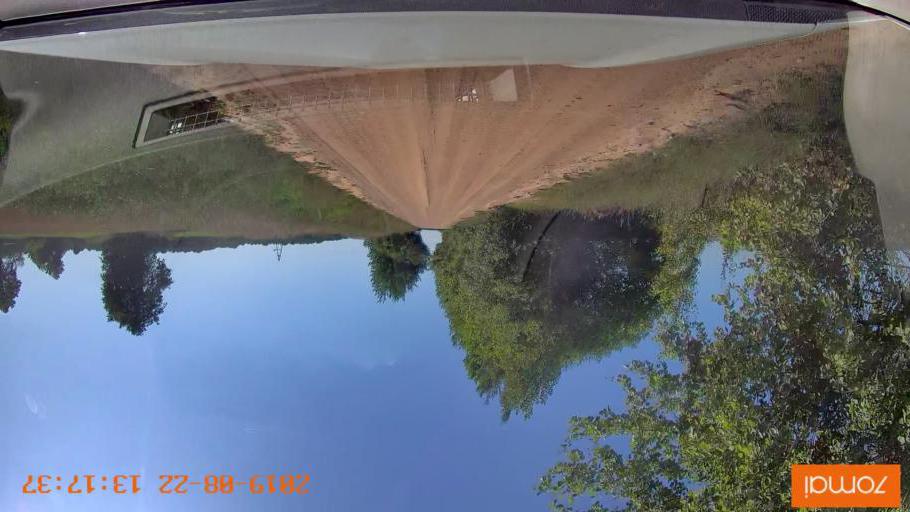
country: BY
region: Minsk
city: Prawdzinski
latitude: 53.2469
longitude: 27.9249
